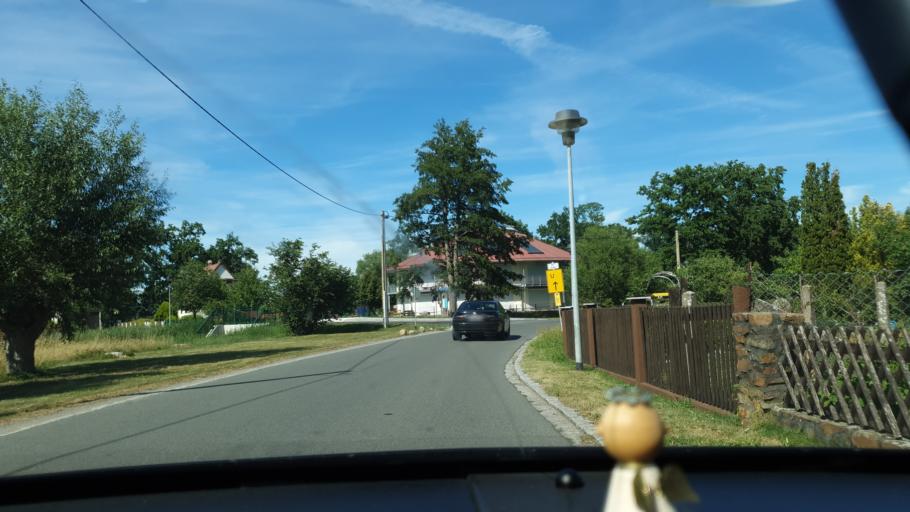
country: DE
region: Saxony
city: Mockrehna
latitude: 51.5001
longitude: 12.8433
